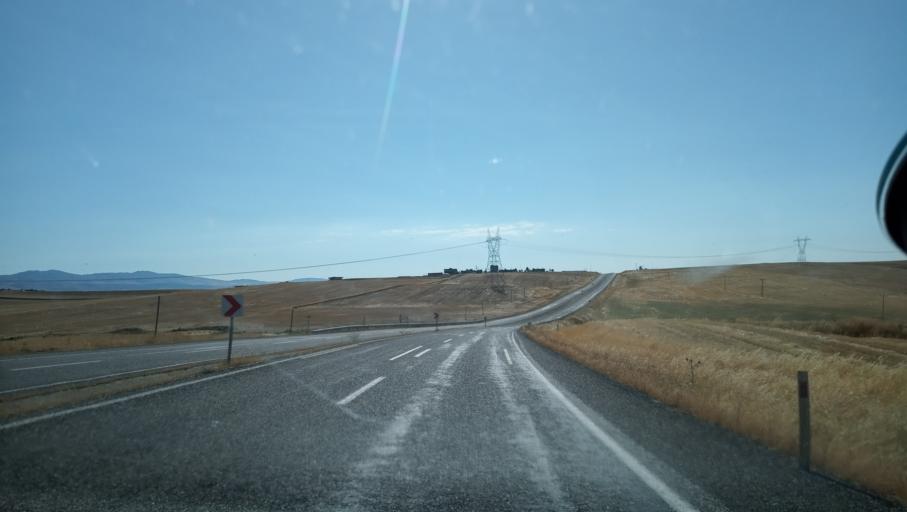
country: TR
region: Diyarbakir
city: Bagdere
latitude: 38.1309
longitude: 40.7643
